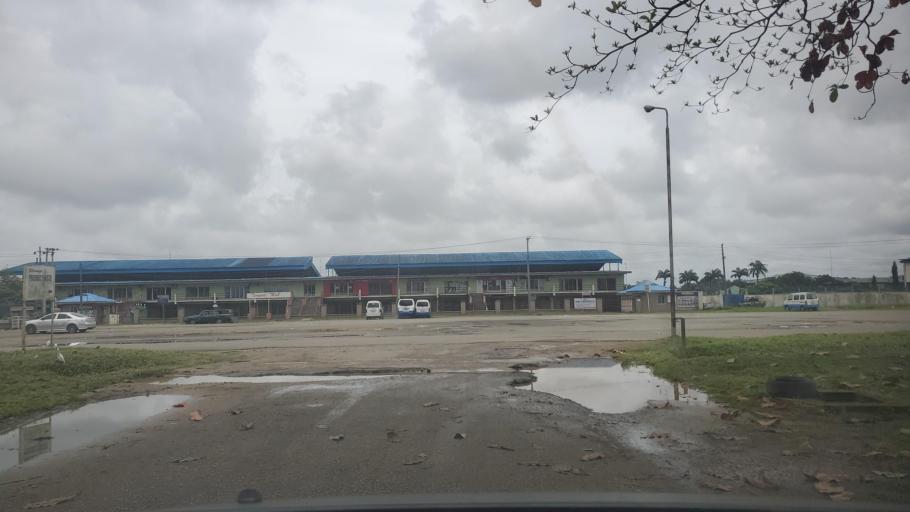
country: NG
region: Rivers
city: Emuoha
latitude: 4.8998
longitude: 6.9221
